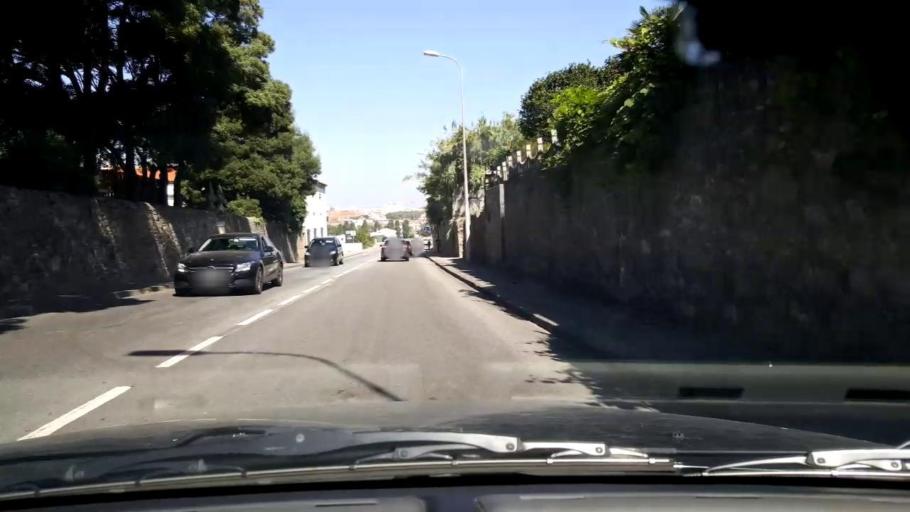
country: PT
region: Porto
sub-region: Vila do Conde
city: Vila do Conde
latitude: 41.3461
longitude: -8.7377
